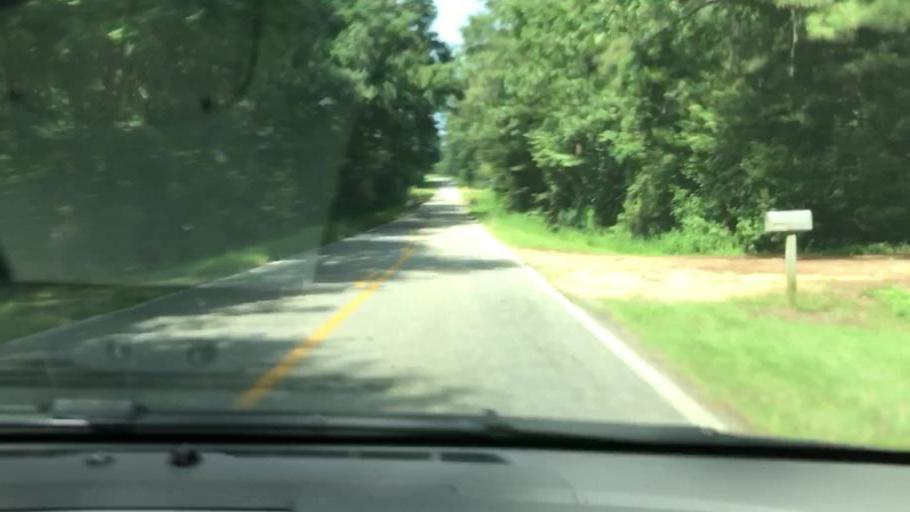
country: US
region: Georgia
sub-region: Seminole County
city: Donalsonville
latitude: 31.1509
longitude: -84.9948
